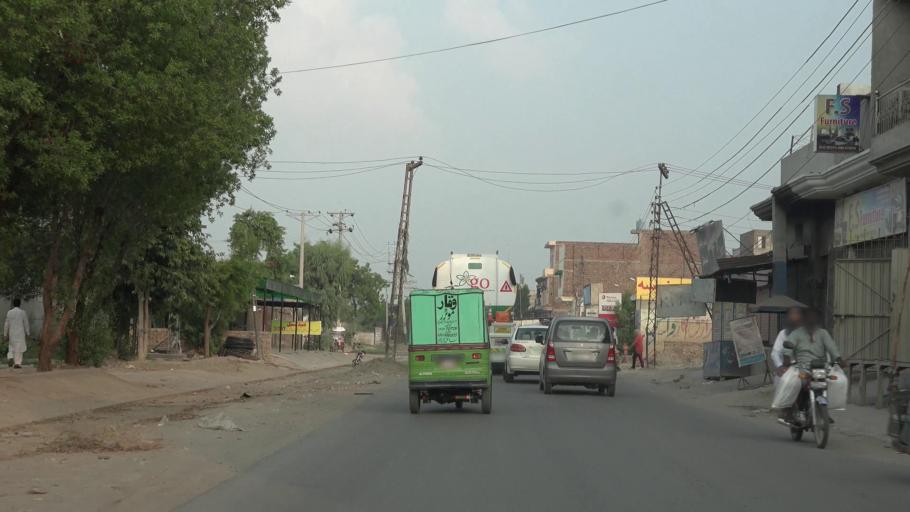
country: PK
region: Punjab
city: Faisalabad
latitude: 31.4492
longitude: 73.1239
